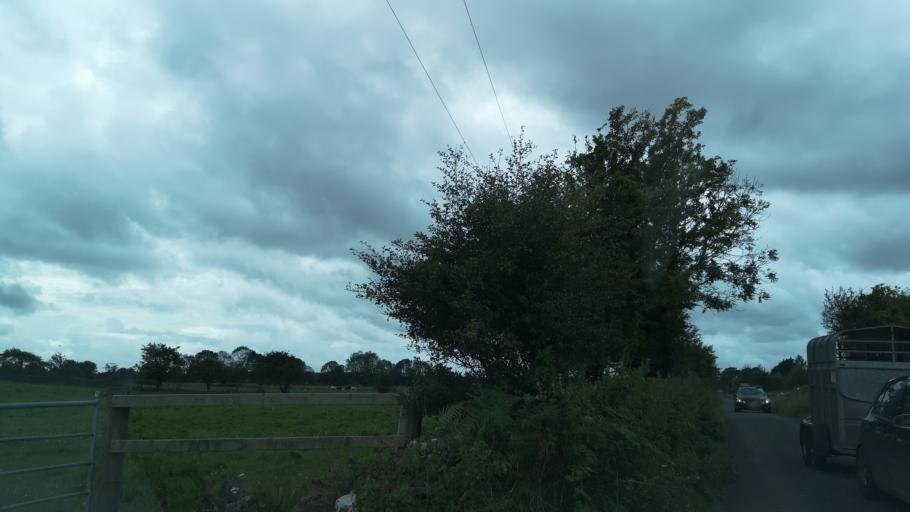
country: IE
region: Connaught
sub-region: County Galway
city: Athenry
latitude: 53.3241
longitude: -8.7492
